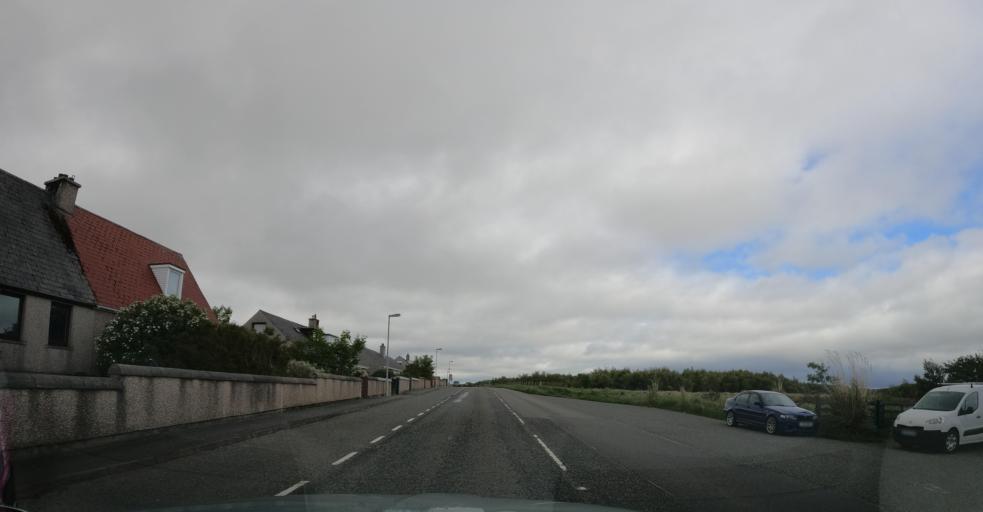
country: GB
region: Scotland
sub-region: Eilean Siar
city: Stornoway
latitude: 58.1560
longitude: -6.4974
